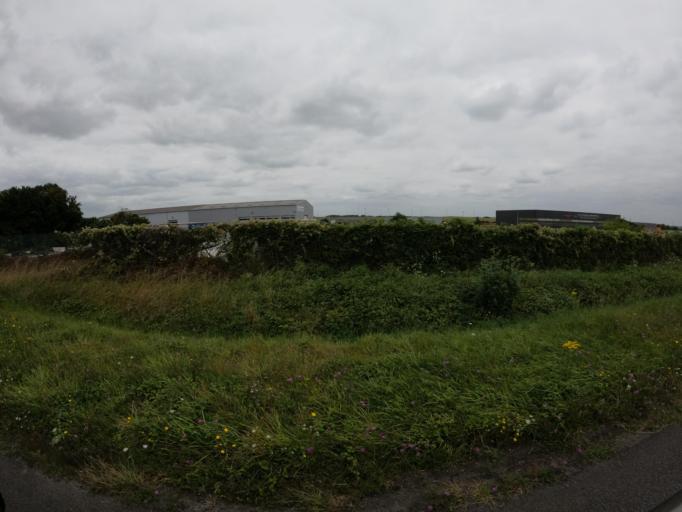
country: FR
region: Pays de la Loire
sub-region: Departement de la Vendee
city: Maillezais
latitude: 46.4208
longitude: -0.7087
